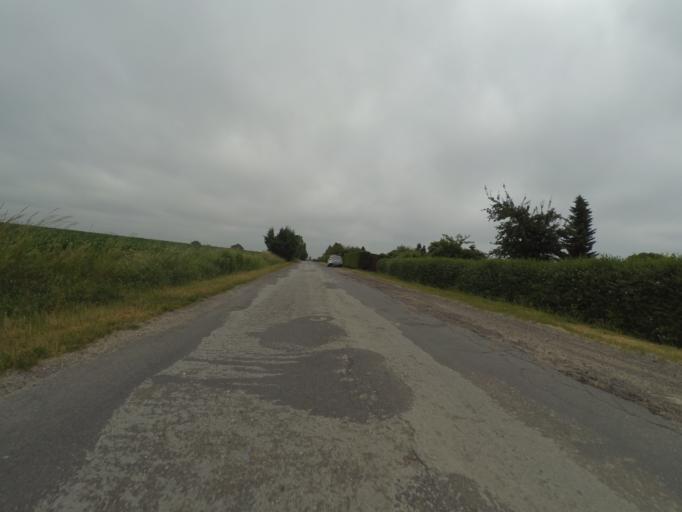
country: DE
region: Mecklenburg-Vorpommern
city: Plau am See
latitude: 53.4605
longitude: 12.2535
